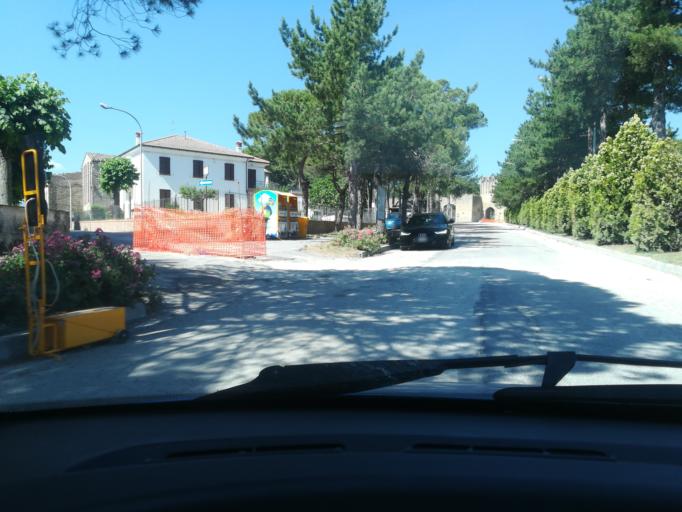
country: IT
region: The Marches
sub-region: Provincia di Macerata
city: San Ginesio
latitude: 43.1070
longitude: 13.3257
